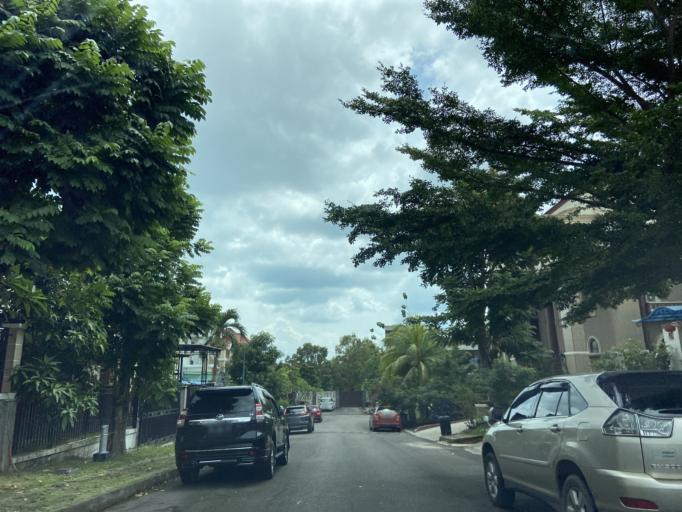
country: SG
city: Singapore
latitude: 1.1295
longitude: 103.9960
